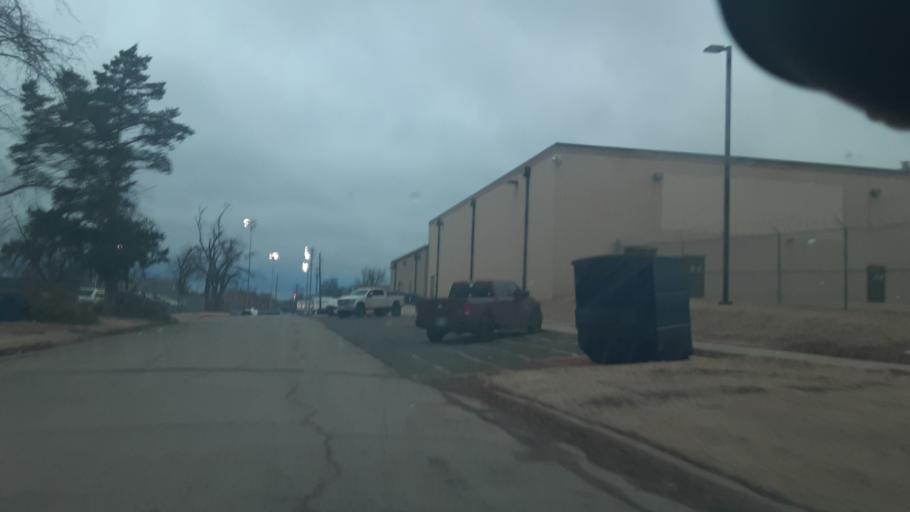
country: US
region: Oklahoma
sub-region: Logan County
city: Guthrie
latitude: 35.8760
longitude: -97.4216
